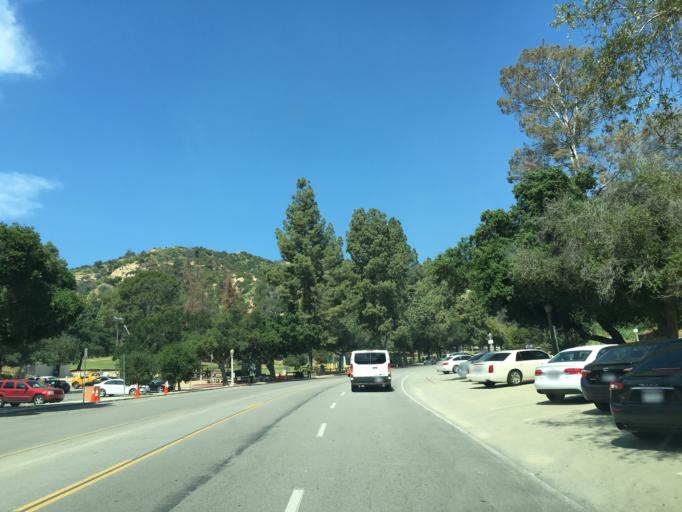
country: US
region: California
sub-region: Los Angeles County
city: Hollywood
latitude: 34.1215
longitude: -118.2966
